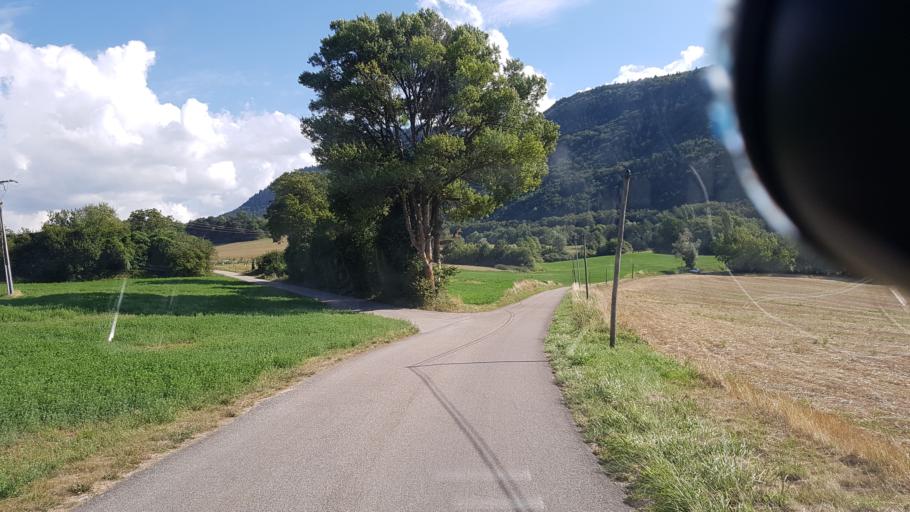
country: FR
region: Rhone-Alpes
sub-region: Departement de l'Isere
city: Mens
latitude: 44.8611
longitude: 5.6909
